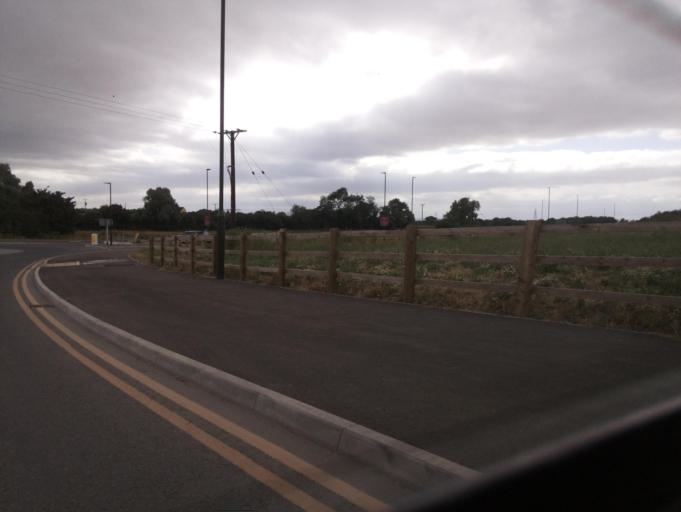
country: GB
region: England
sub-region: Worcestershire
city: Bredon
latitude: 51.9962
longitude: -2.1105
